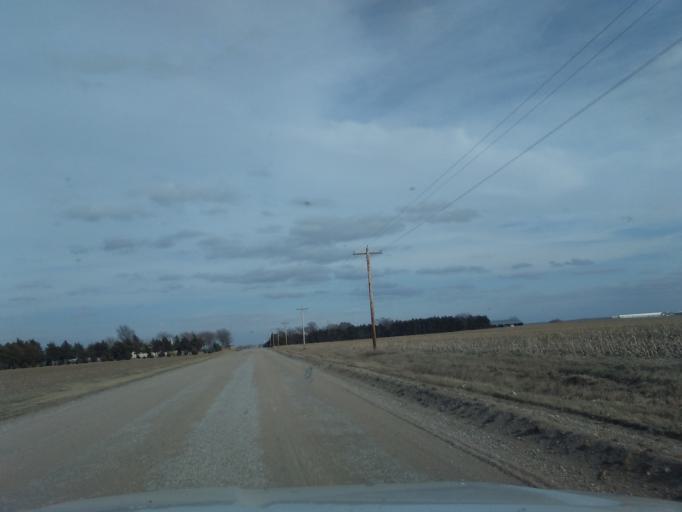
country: US
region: Nebraska
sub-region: Gage County
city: Beatrice
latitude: 40.3210
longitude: -96.8588
